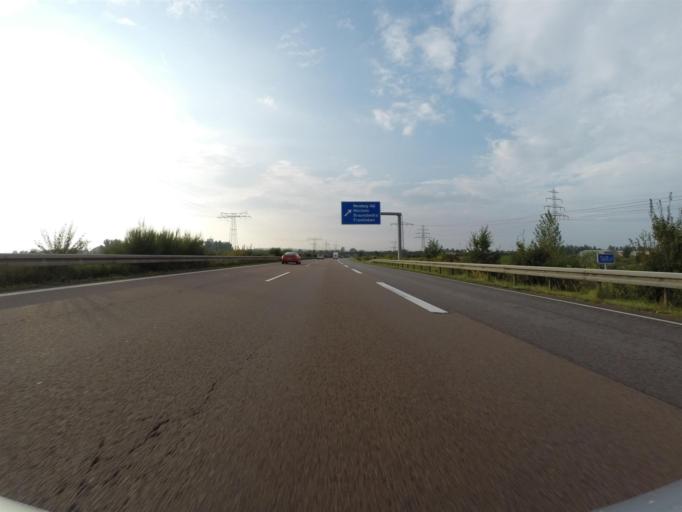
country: DE
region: Saxony-Anhalt
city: Beuna
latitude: 51.3075
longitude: 11.9547
